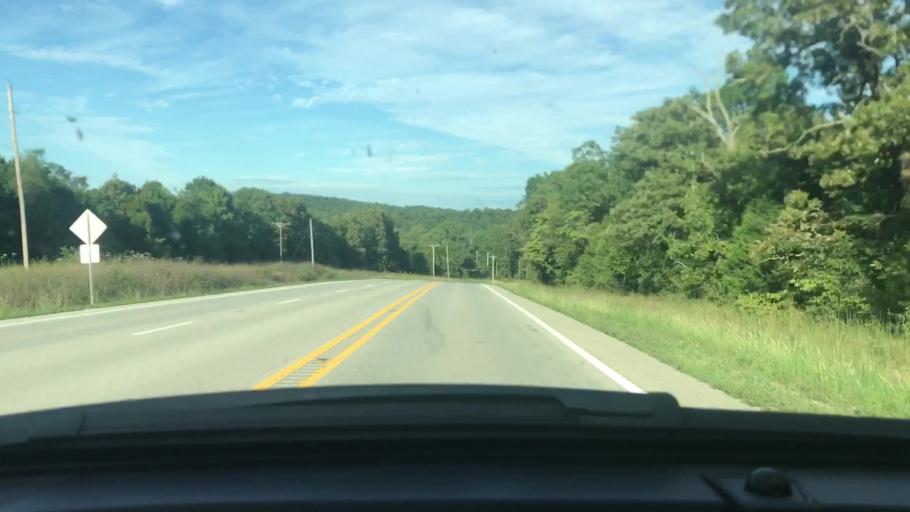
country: US
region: Arkansas
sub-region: Sharp County
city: Cherokee Village
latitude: 36.2742
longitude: -91.3634
